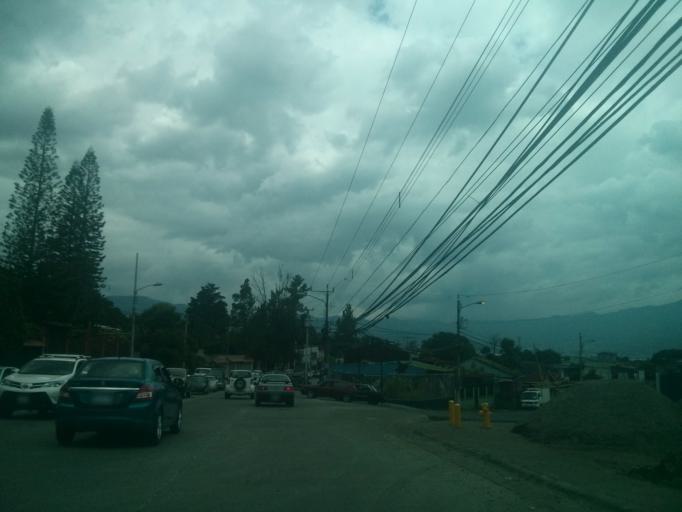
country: CR
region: San Jose
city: San Pedro
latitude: 9.9179
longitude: -84.0544
